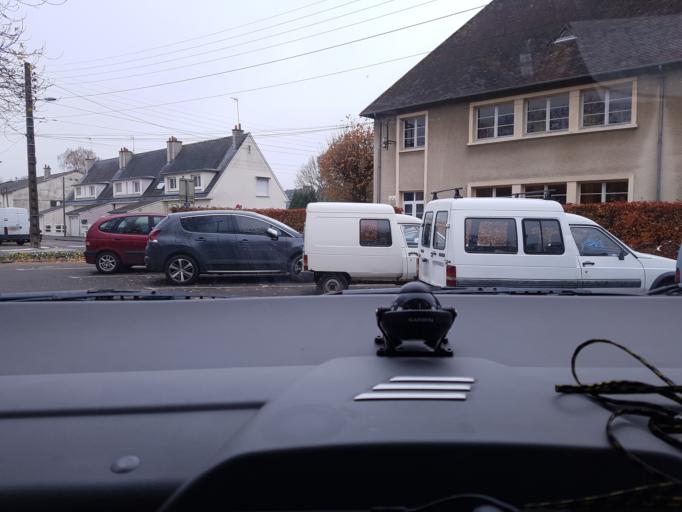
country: FR
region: Lower Normandy
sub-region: Departement du Calvados
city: Conde-sur-Noireau
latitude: 48.8508
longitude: -0.5536
